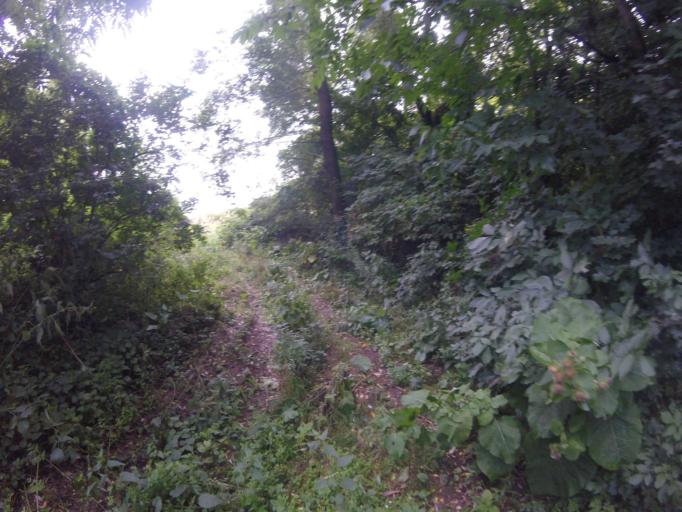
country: SK
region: Nitriansky
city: Sahy
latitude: 48.0489
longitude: 18.9247
